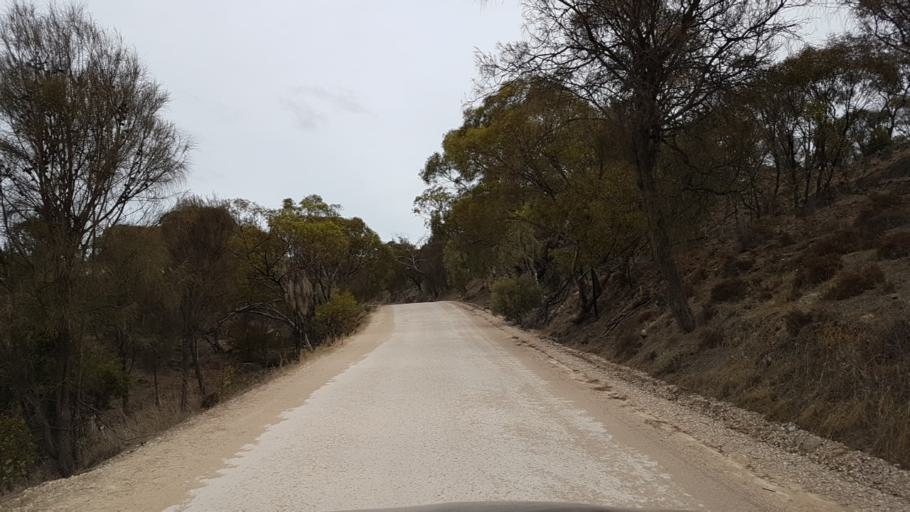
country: AU
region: South Australia
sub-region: Mount Barker
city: Callington
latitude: -35.0041
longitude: 139.0847
